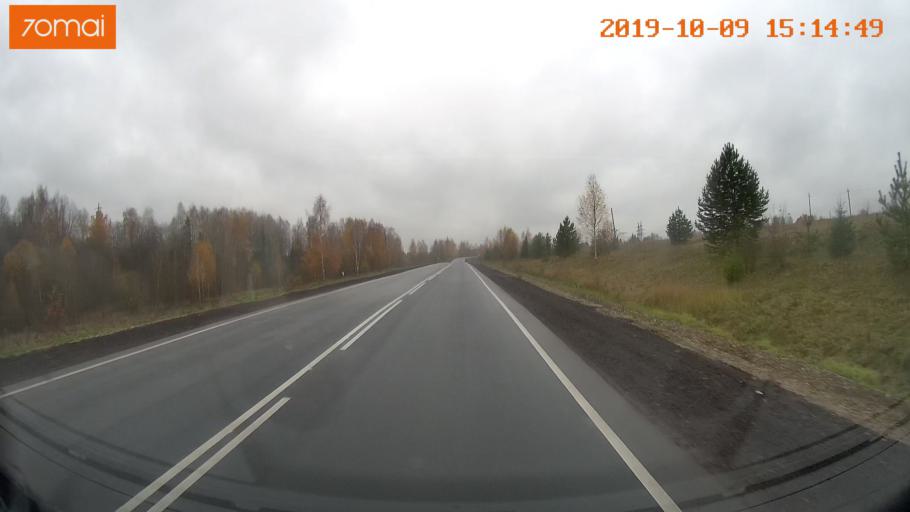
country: RU
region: Kostroma
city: Susanino
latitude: 58.1294
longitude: 41.6000
